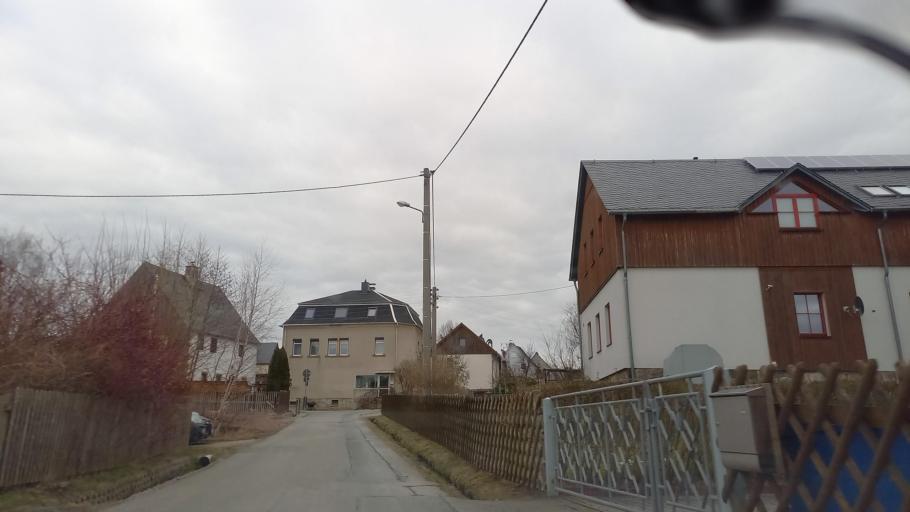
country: DE
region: Saxony
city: Kirchberg
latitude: 50.6286
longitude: 12.5536
